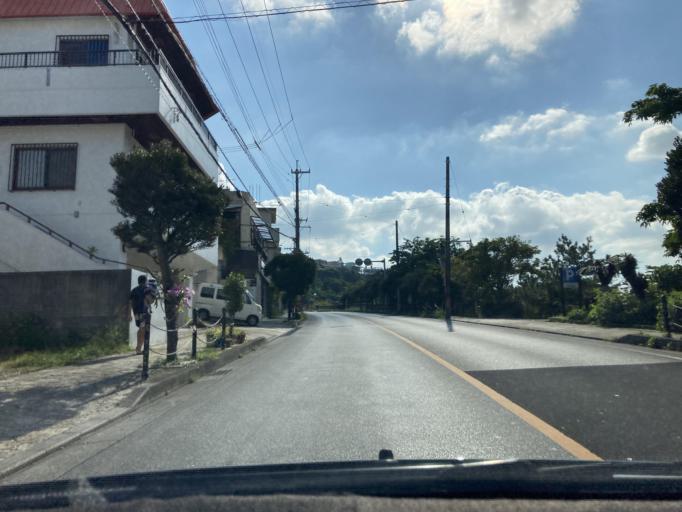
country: JP
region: Okinawa
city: Naha-shi
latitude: 26.2134
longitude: 127.7168
